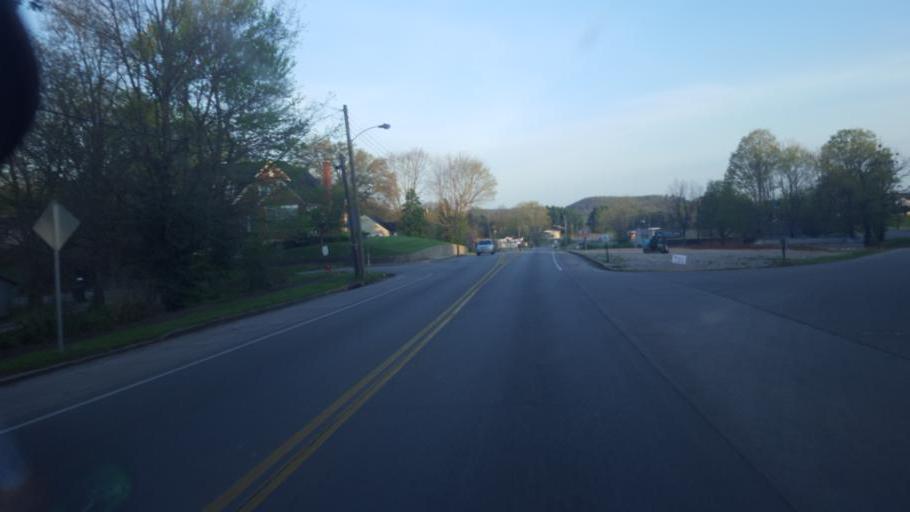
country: US
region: Kentucky
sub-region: Hart County
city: Munfordville
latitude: 37.2728
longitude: -85.8923
